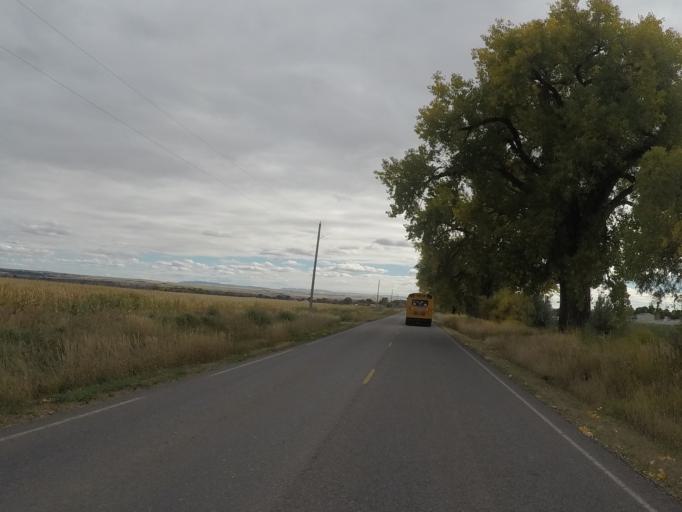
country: US
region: Montana
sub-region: Yellowstone County
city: Laurel
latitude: 45.7523
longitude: -108.6589
